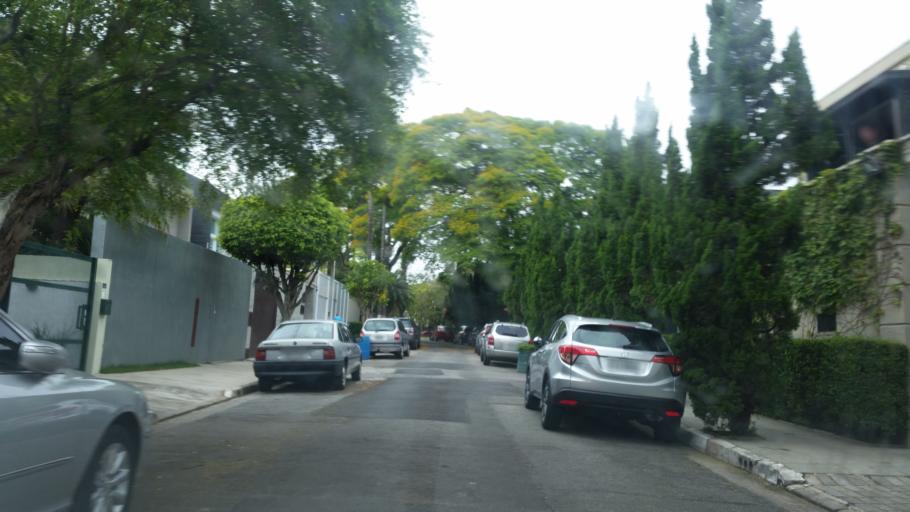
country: BR
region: Sao Paulo
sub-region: Sao Paulo
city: Sao Paulo
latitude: -23.5943
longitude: -46.6566
